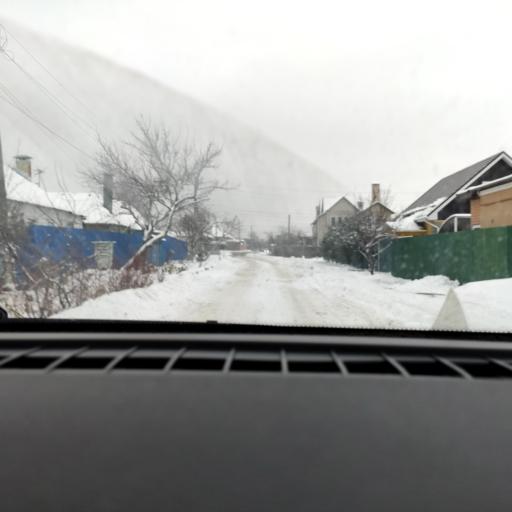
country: RU
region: Voronezj
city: Maslovka
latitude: 51.6114
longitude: 39.2207
